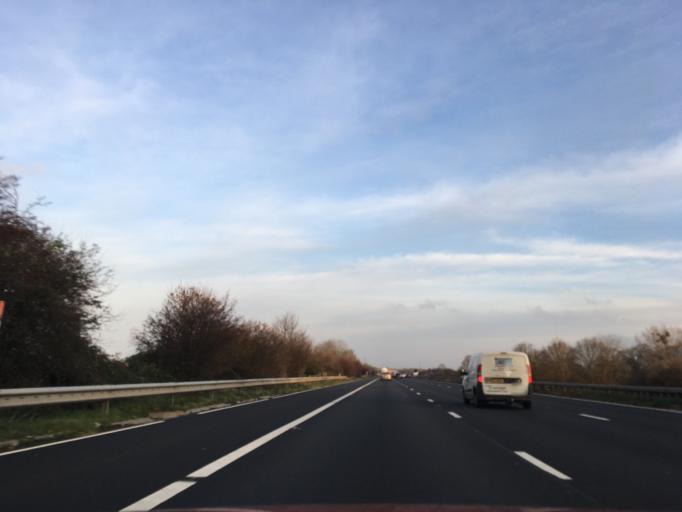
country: GB
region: England
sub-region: Gloucestershire
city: Tewkesbury
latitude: 51.9842
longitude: -2.1258
